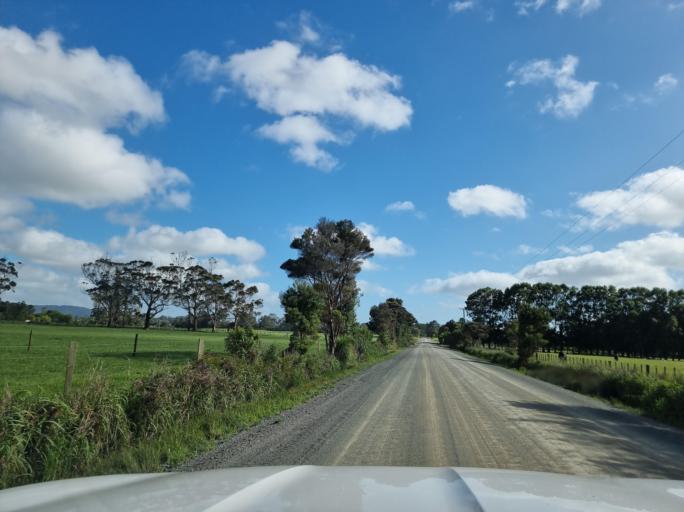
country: NZ
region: Auckland
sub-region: Auckland
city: Wellsford
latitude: -36.1321
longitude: 174.5921
